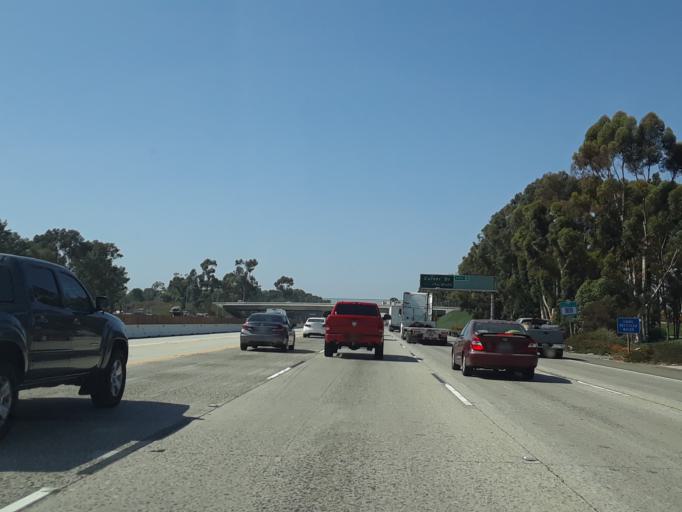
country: US
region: California
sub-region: Orange County
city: Irvine
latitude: 33.6631
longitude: -117.7912
